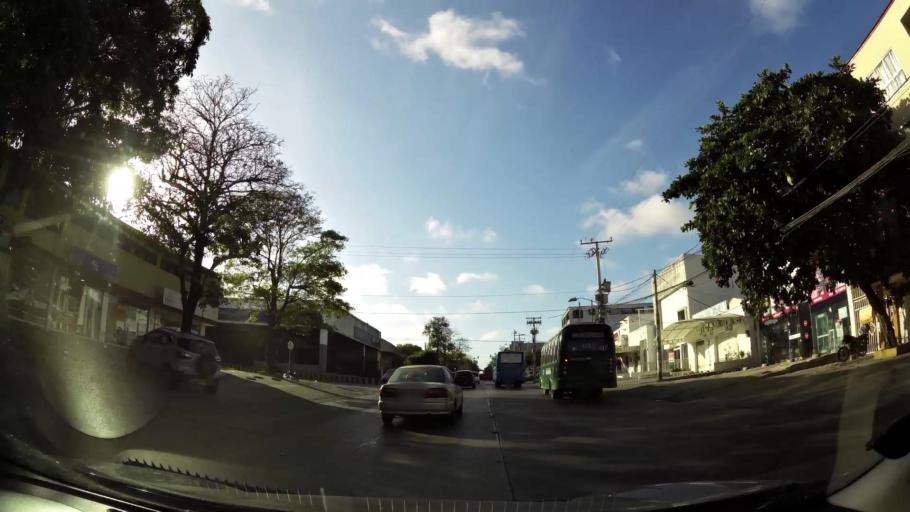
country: CO
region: Atlantico
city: Barranquilla
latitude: 10.9899
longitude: -74.8040
